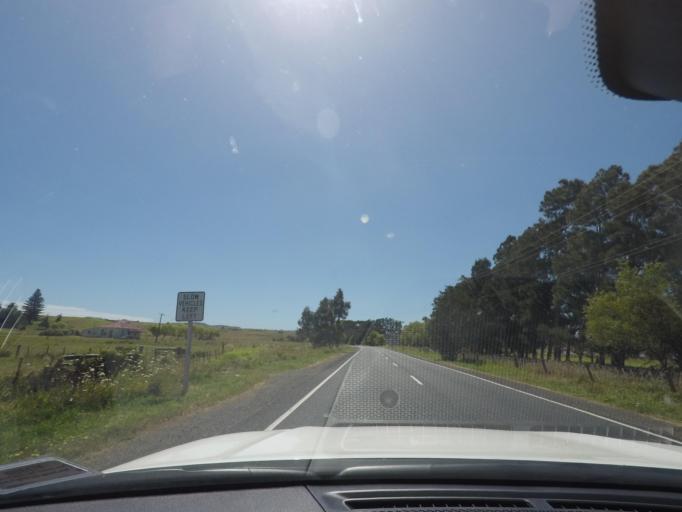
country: NZ
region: Auckland
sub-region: Auckland
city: Parakai
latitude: -36.6366
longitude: 174.3841
